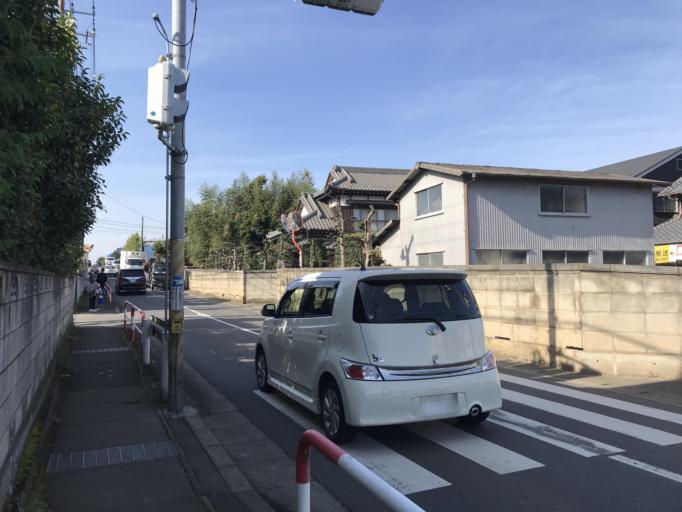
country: JP
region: Chiba
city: Shiroi
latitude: 35.7839
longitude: 139.9937
